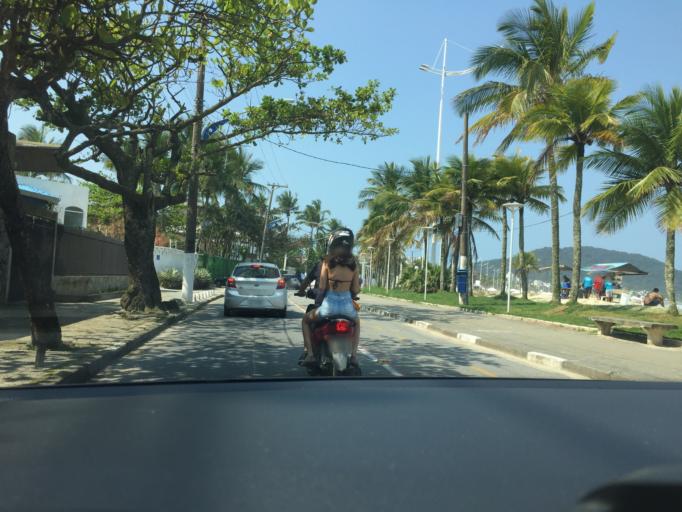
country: BR
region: Sao Paulo
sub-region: Guaruja
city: Guaruja
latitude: -23.9852
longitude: -46.2204
